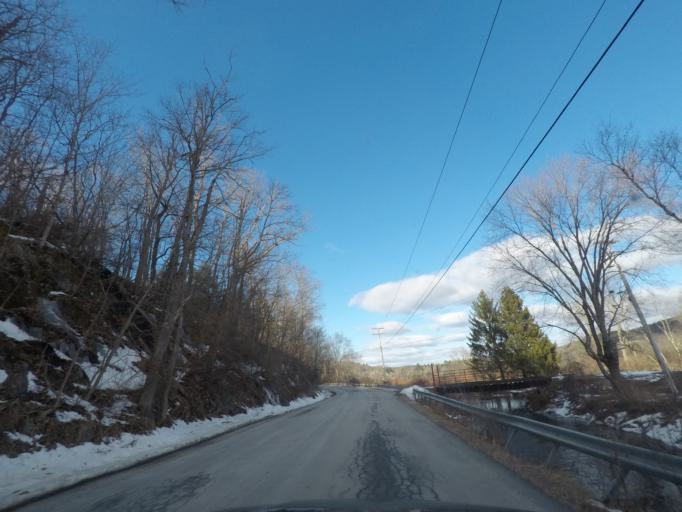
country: US
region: New York
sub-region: Rensselaer County
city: Nassau
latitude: 42.5394
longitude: -73.5289
